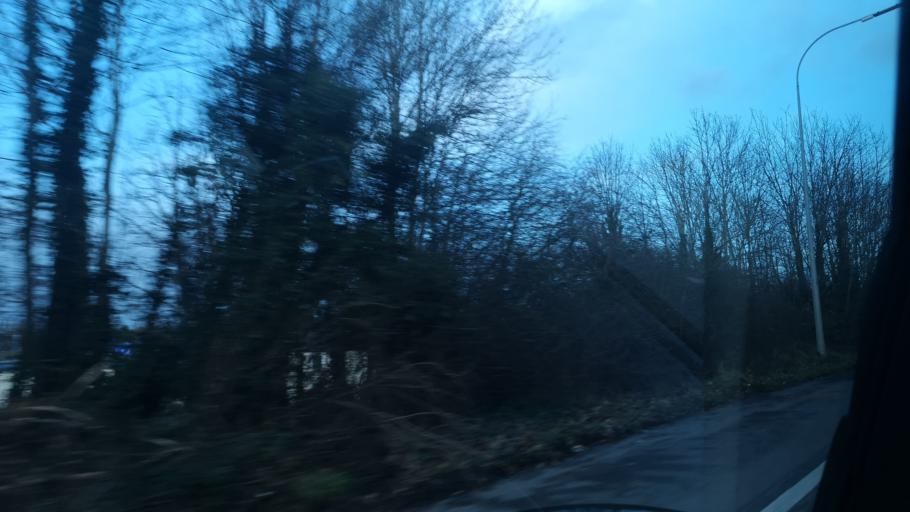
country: GB
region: Northern Ireland
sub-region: Newry and Mourne District
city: Newry
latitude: 54.1962
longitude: -6.3436
